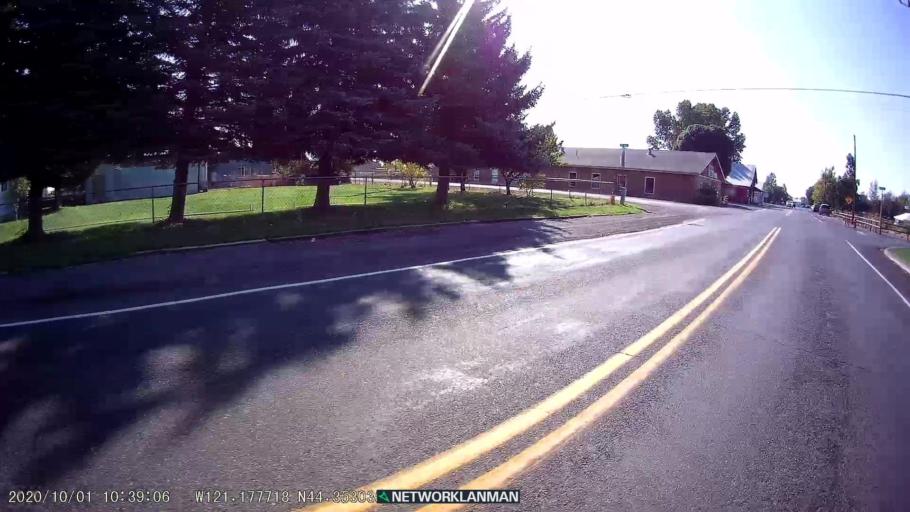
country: US
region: Oregon
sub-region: Deschutes County
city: Terrebonne
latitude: 44.3531
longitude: -121.1777
